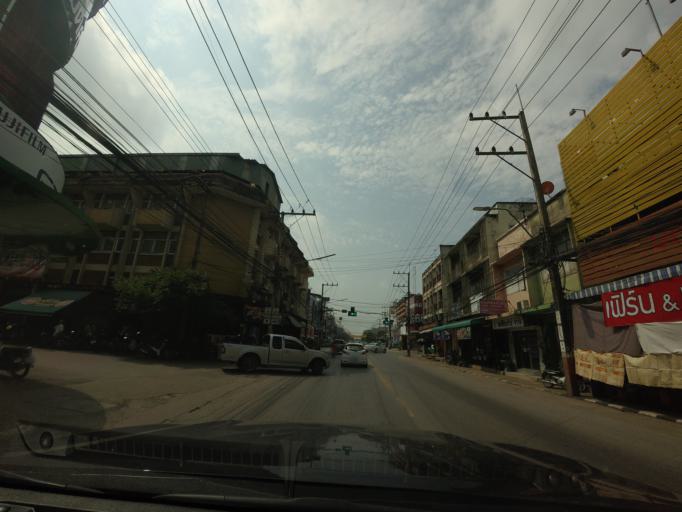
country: TH
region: Phrae
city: Phrae
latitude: 18.1368
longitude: 100.1471
